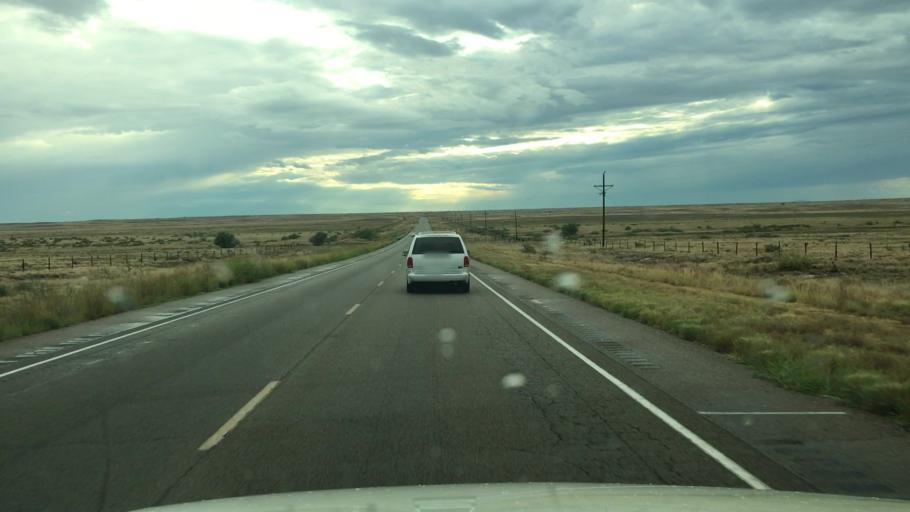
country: US
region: New Mexico
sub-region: Chaves County
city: Dexter
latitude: 33.4069
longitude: -104.2983
